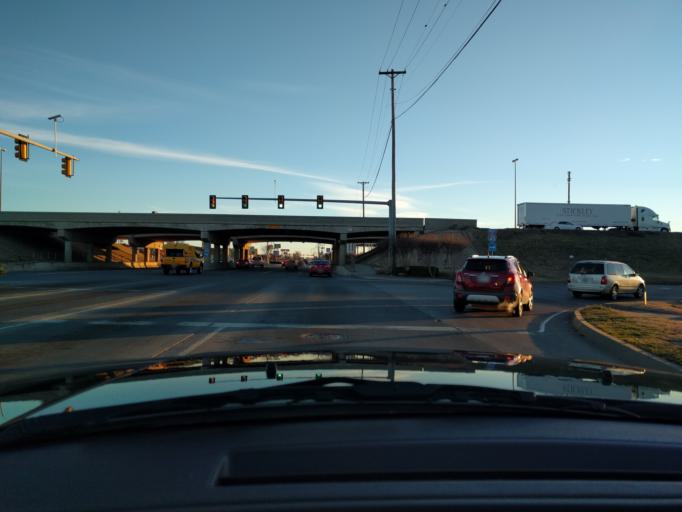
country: US
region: Oklahoma
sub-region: Oklahoma County
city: Warr Acres
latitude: 35.4608
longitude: -97.6013
